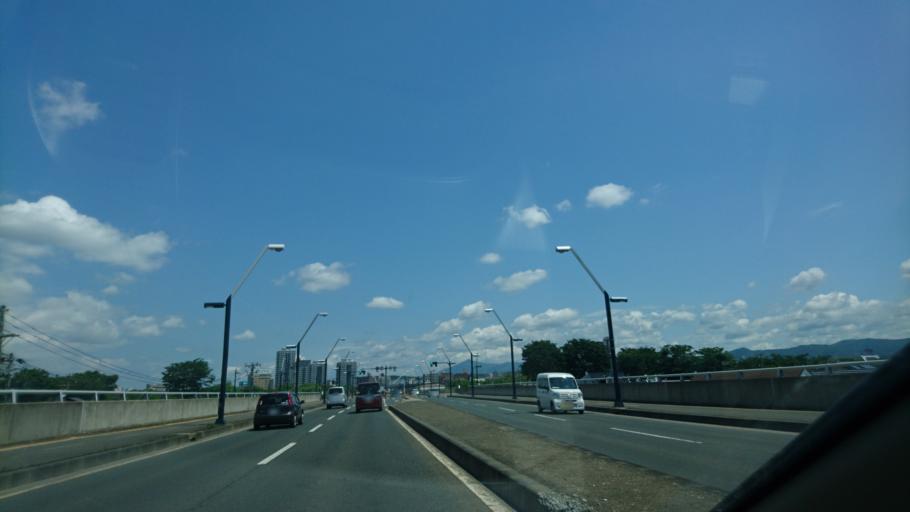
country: JP
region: Iwate
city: Morioka-shi
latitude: 39.6912
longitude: 141.1363
